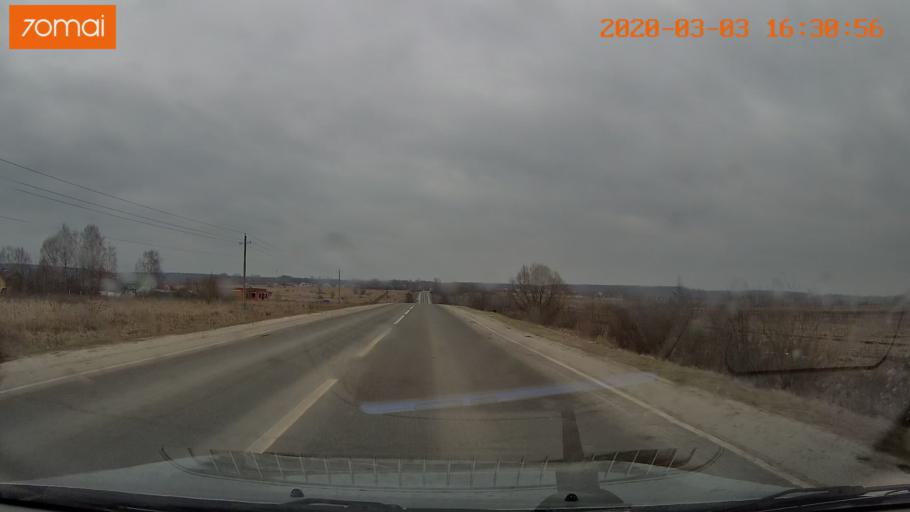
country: RU
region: Moskovskaya
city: Konobeyevo
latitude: 55.4295
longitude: 38.7170
